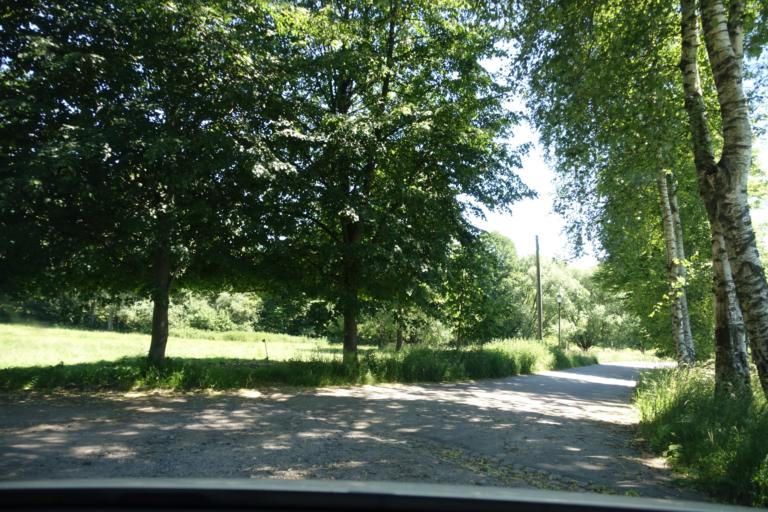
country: DE
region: Saxony
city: Eppendorf
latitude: 50.8235
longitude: 13.2687
